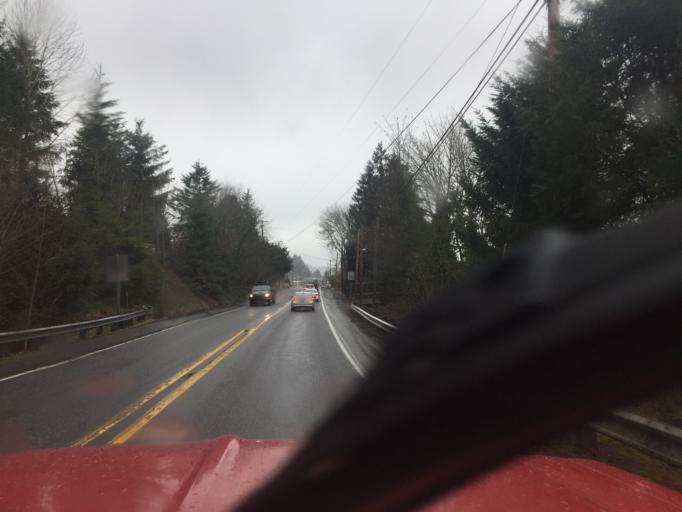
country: US
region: Oregon
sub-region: Columbia County
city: Rainier
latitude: 46.0877
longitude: -122.9286
